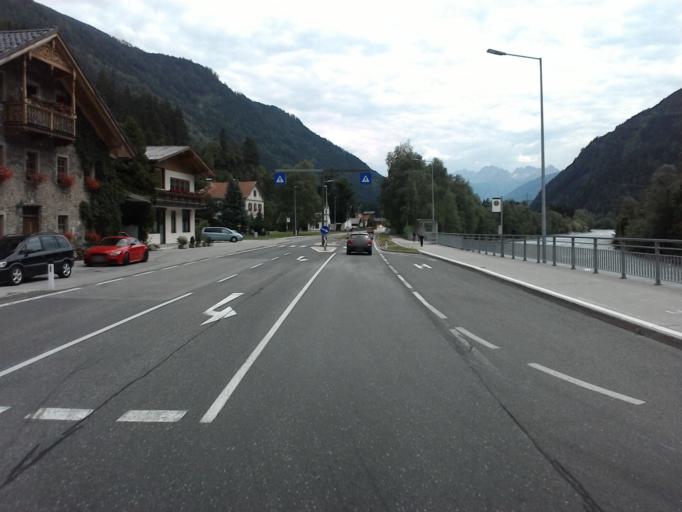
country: AT
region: Tyrol
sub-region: Politischer Bezirk Lienz
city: Schlaiten
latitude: 46.9044
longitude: 12.6297
